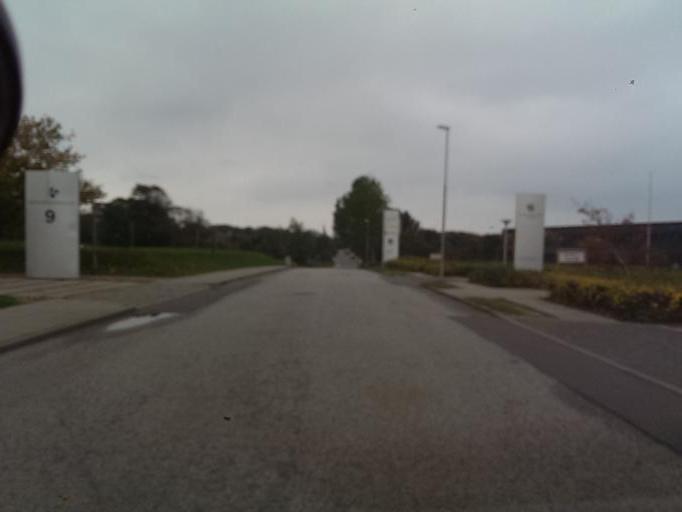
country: DK
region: South Denmark
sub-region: Esbjerg Kommune
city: Esbjerg
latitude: 55.4913
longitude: 8.4485
